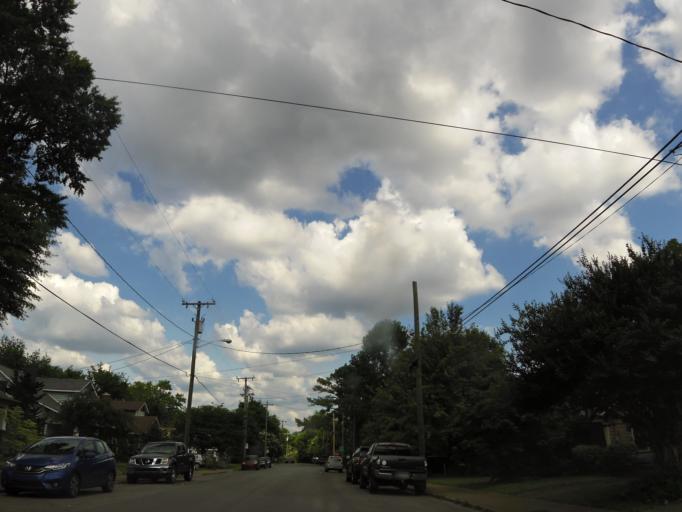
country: US
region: Tennessee
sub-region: Davidson County
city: Nashville
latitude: 36.1730
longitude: -86.7381
